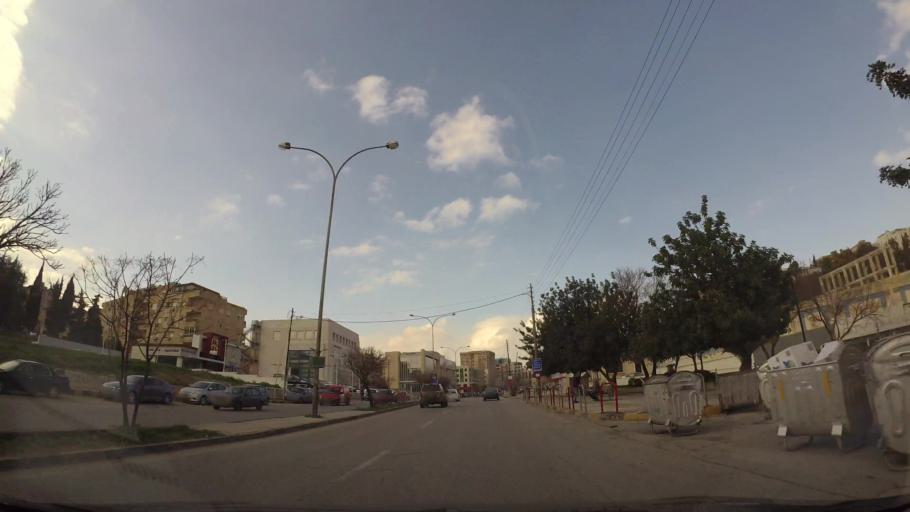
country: JO
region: Amman
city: Al Jubayhah
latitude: 31.9699
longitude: 35.8863
